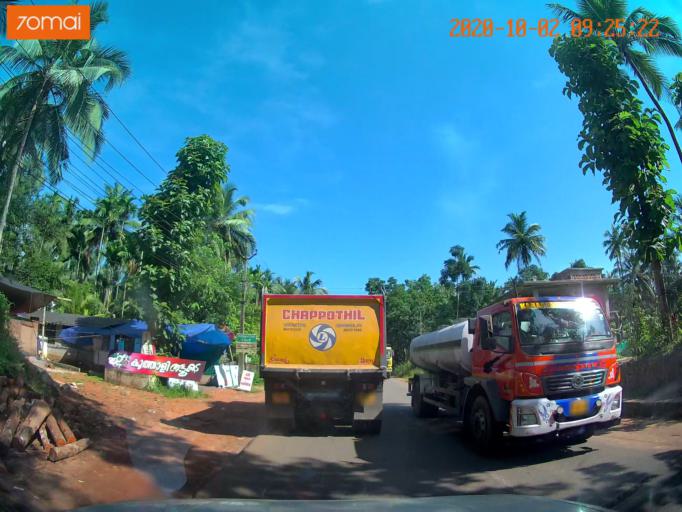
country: IN
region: Kerala
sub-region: Kozhikode
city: Naduvannur
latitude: 11.5878
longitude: 75.7655
